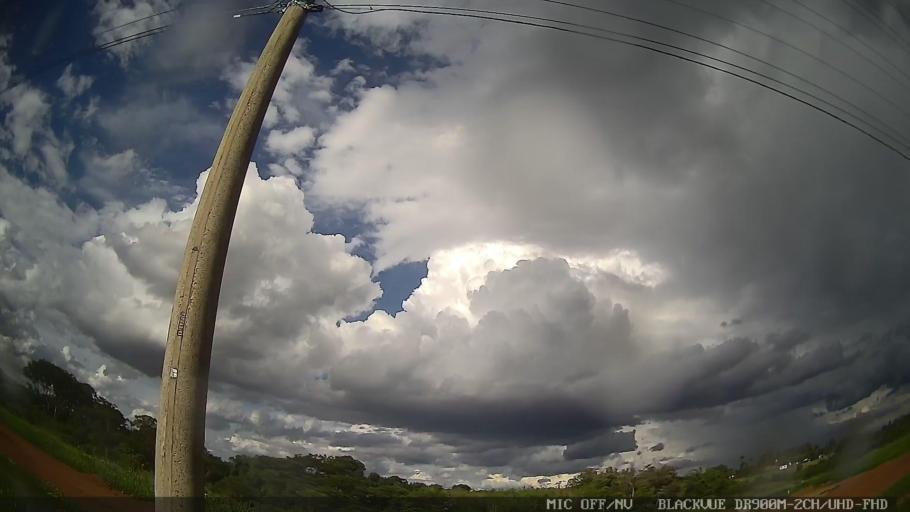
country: BR
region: Sao Paulo
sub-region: Jaguariuna
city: Jaguariuna
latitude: -22.6710
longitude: -47.0298
